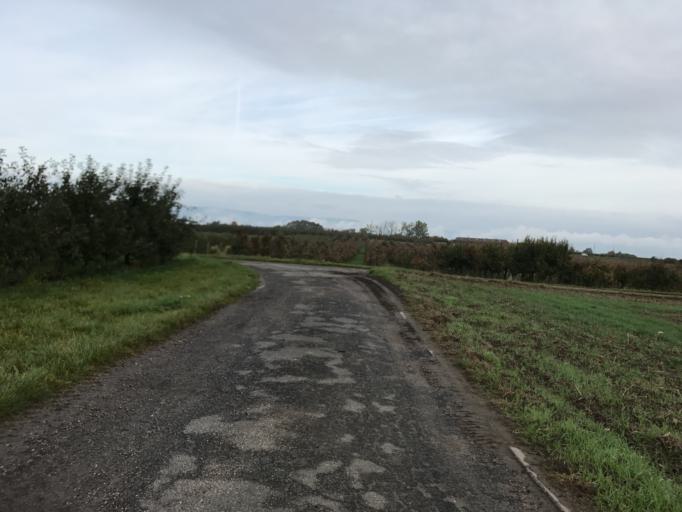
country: DE
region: Rheinland-Pfalz
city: Wackernheim
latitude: 49.9714
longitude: 8.1052
